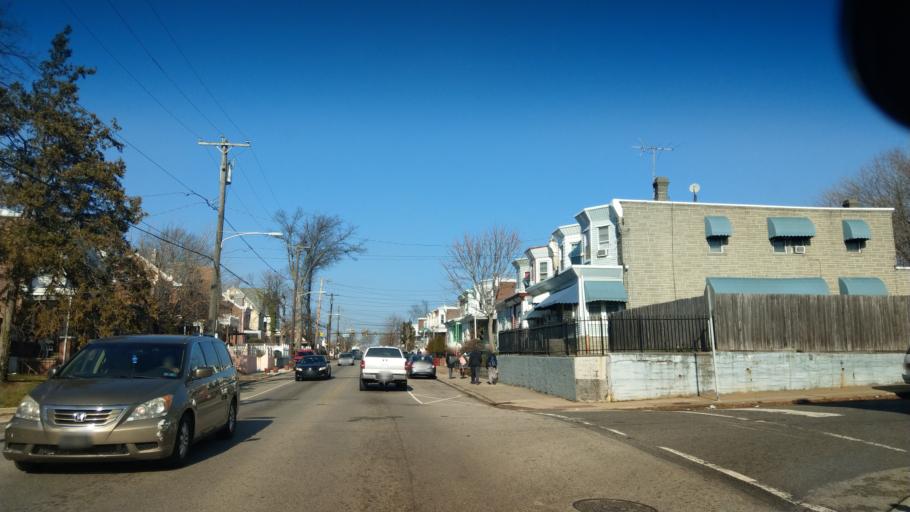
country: US
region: Pennsylvania
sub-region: Montgomery County
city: Rockledge
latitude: 40.0339
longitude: -75.1240
